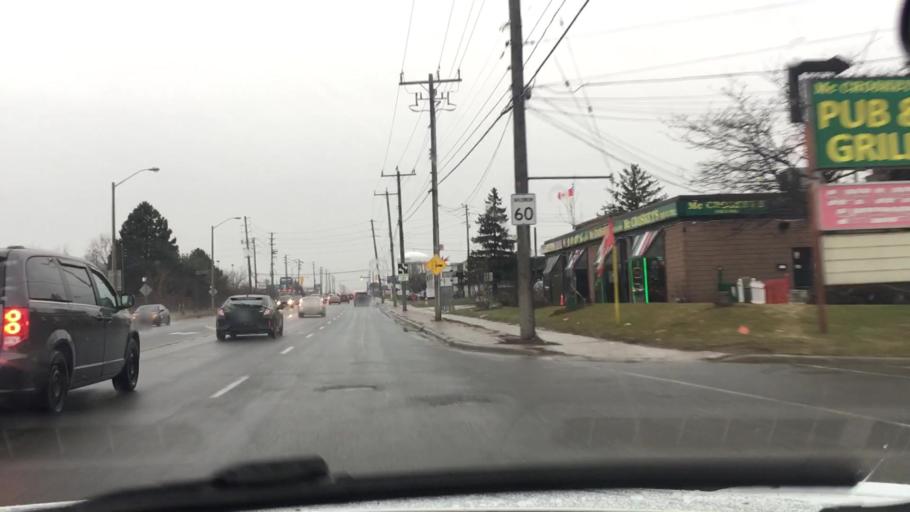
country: CA
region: Ontario
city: Scarborough
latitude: 43.7196
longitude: -79.2841
